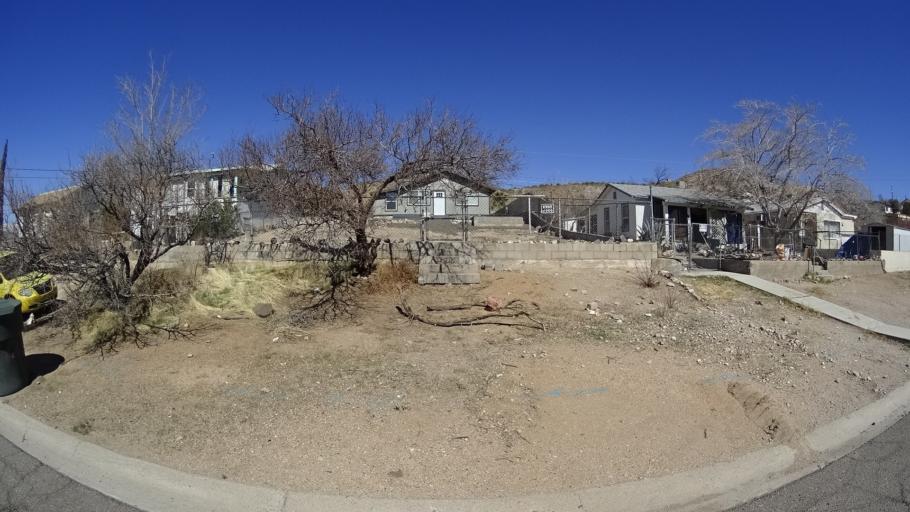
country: US
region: Arizona
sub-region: Mohave County
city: Kingman
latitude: 35.1932
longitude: -114.0549
